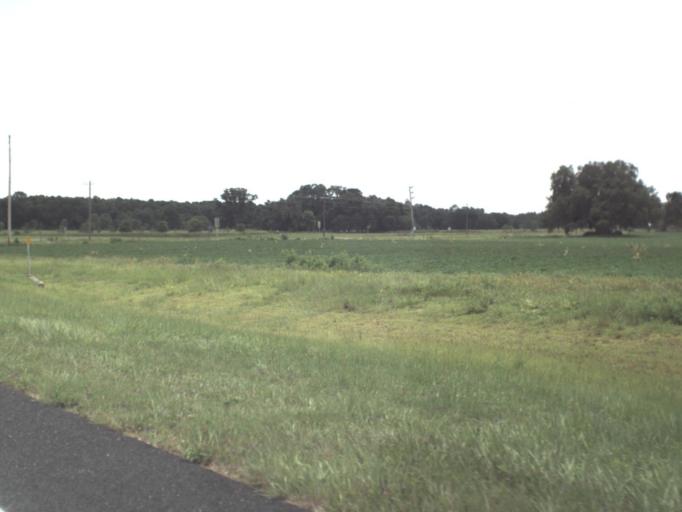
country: US
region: Florida
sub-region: Levy County
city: Williston
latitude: 29.3974
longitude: -82.4954
